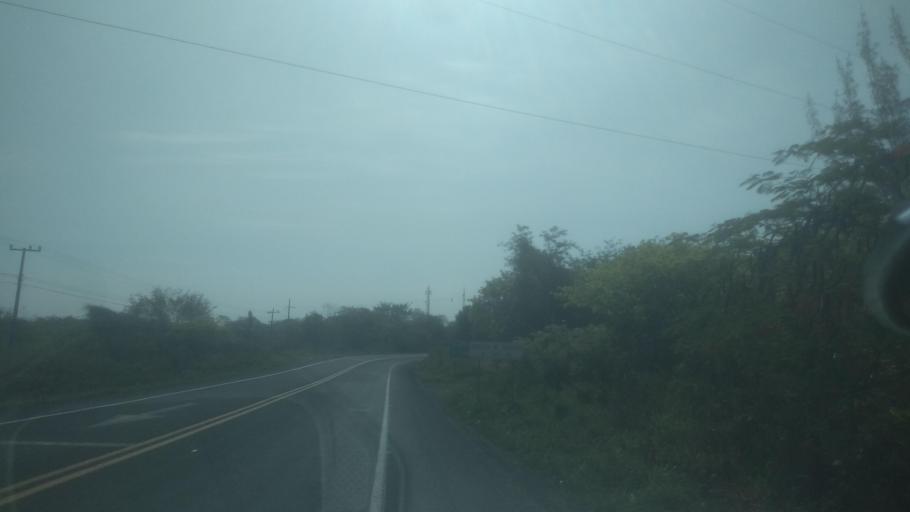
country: MX
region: Veracruz
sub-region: Emiliano Zapata
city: Plan del Rio
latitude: 19.3932
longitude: -96.6257
